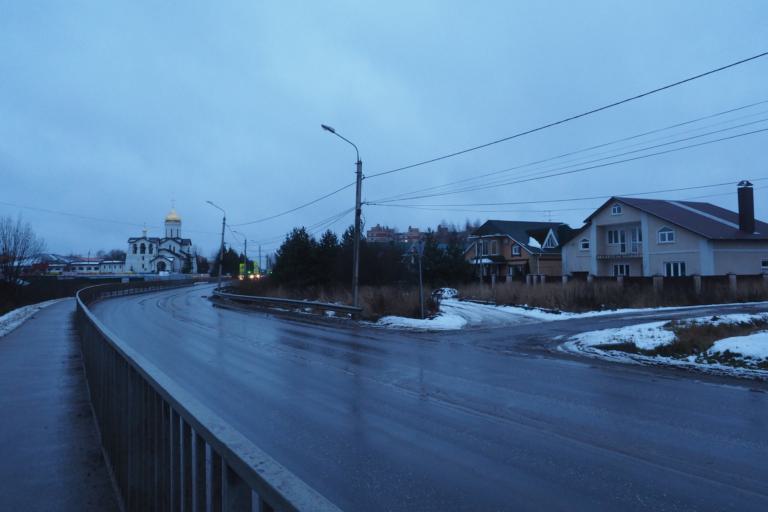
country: RU
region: Moskovskaya
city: Sergiyev Posad
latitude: 56.3394
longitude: 38.1350
